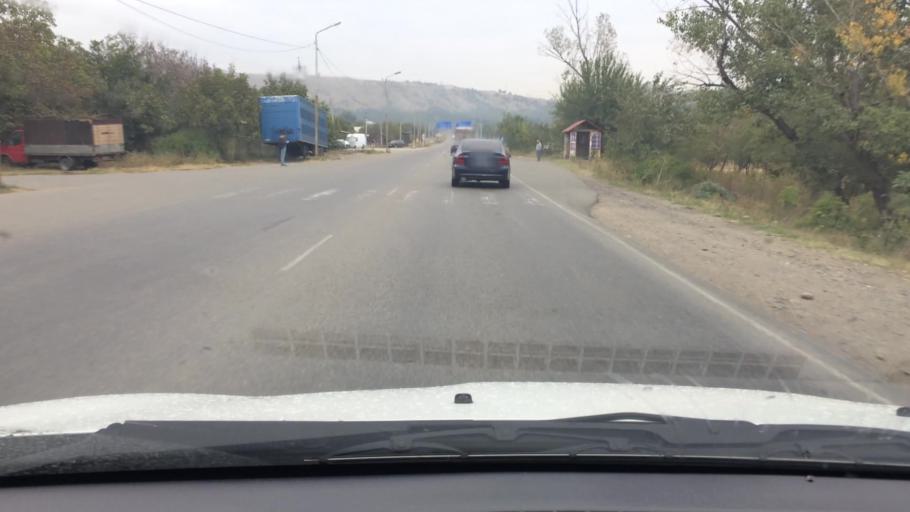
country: GE
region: T'bilisi
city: Tbilisi
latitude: 41.6124
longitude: 44.7883
